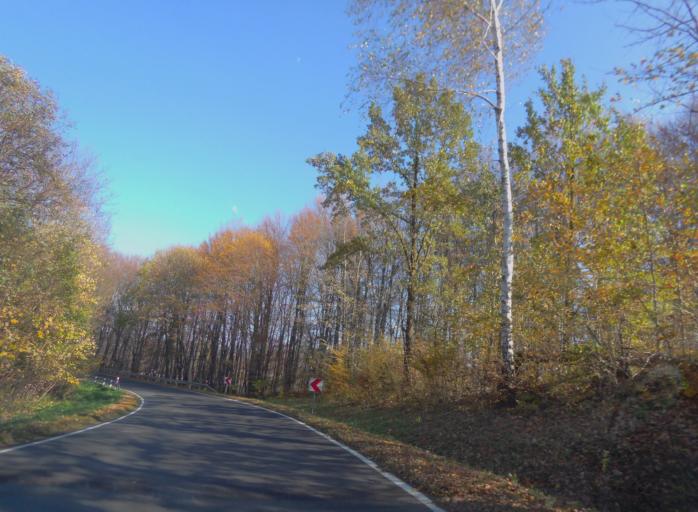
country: PL
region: Subcarpathian Voivodeship
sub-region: Powiat leski
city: Polanczyk
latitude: 49.3915
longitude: 22.4333
